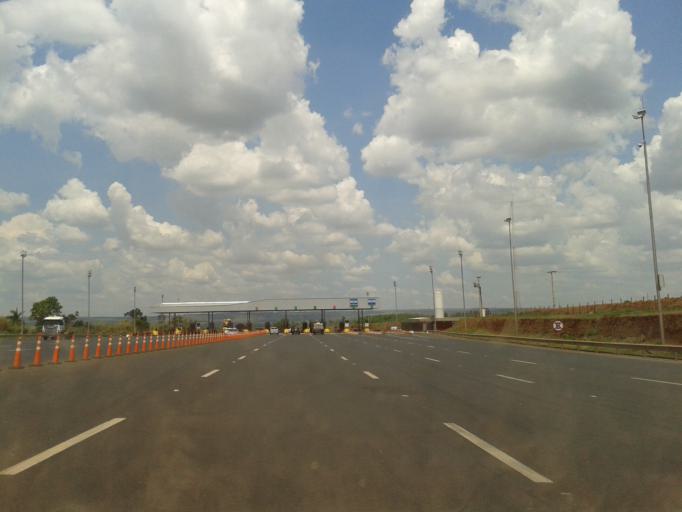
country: BR
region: Minas Gerais
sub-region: Araguari
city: Araguari
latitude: -18.7487
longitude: -48.2343
